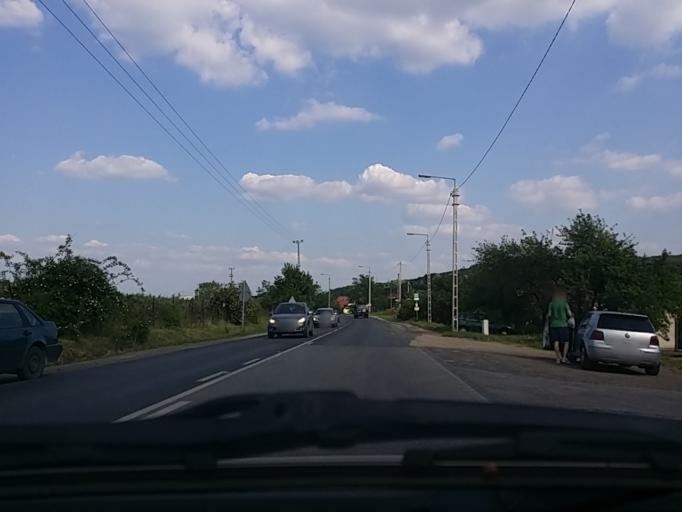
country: HU
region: Pest
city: Nagykovacsi
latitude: 47.6520
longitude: 18.9907
